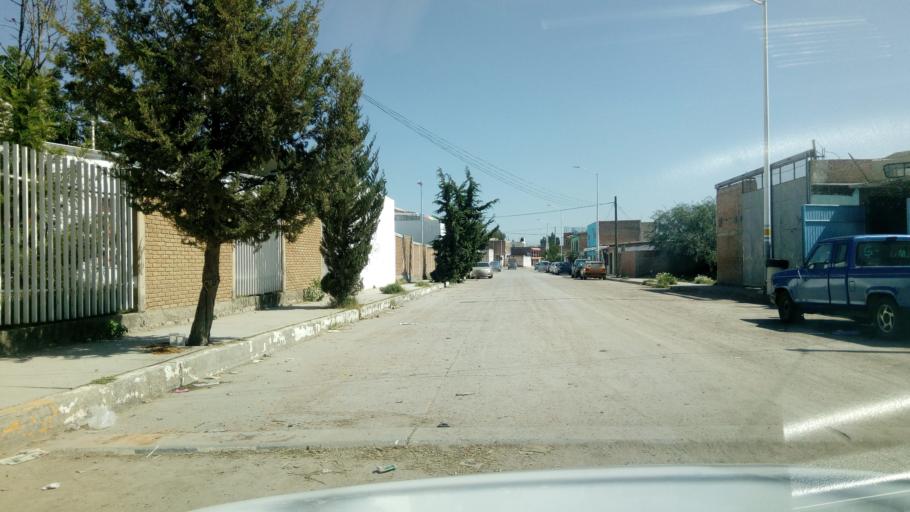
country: MX
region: Durango
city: Victoria de Durango
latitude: 23.9887
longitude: -104.6802
